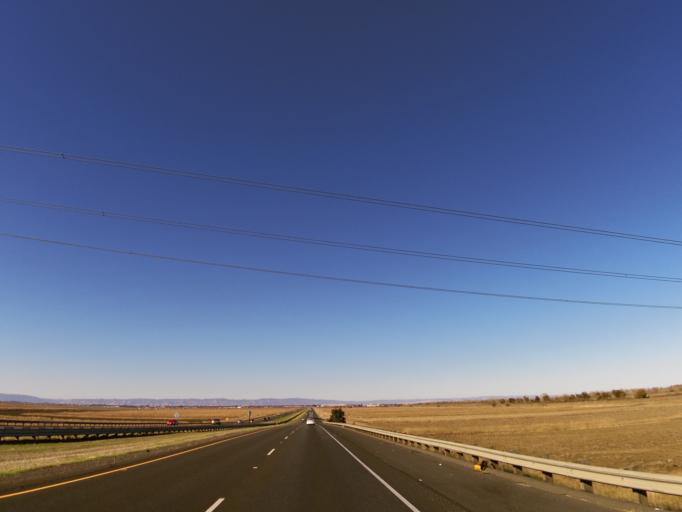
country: US
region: California
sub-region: Yolo County
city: Woodland
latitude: 38.6737
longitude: -121.6734
